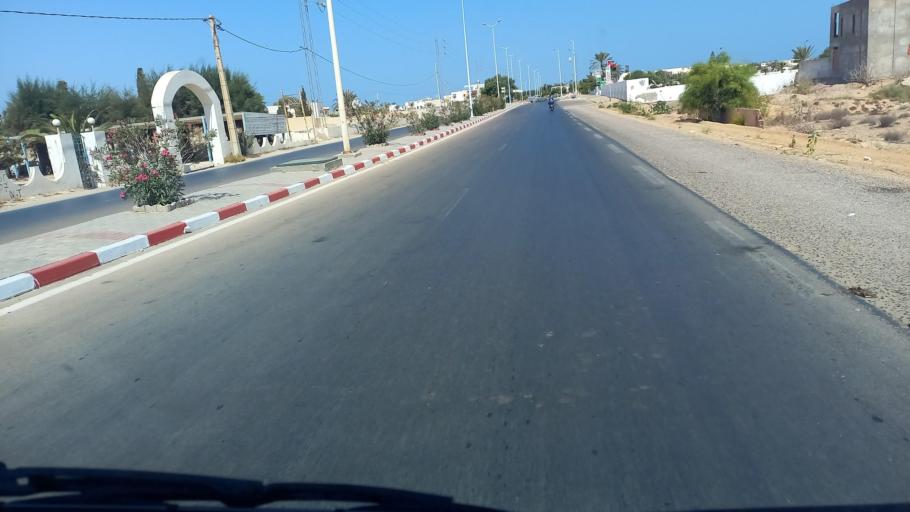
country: TN
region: Madanin
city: Midoun
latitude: 33.8570
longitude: 10.9768
